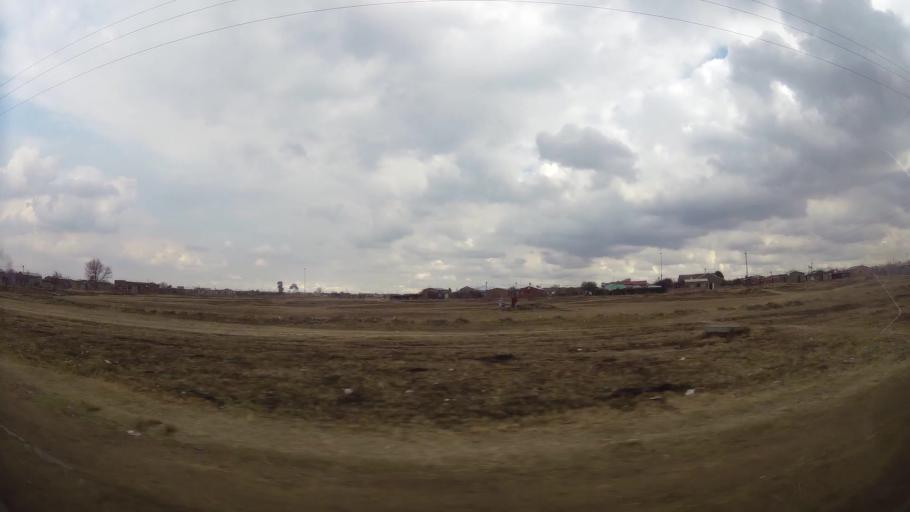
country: ZA
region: Orange Free State
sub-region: Fezile Dabi District Municipality
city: Sasolburg
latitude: -26.8554
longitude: 27.8805
